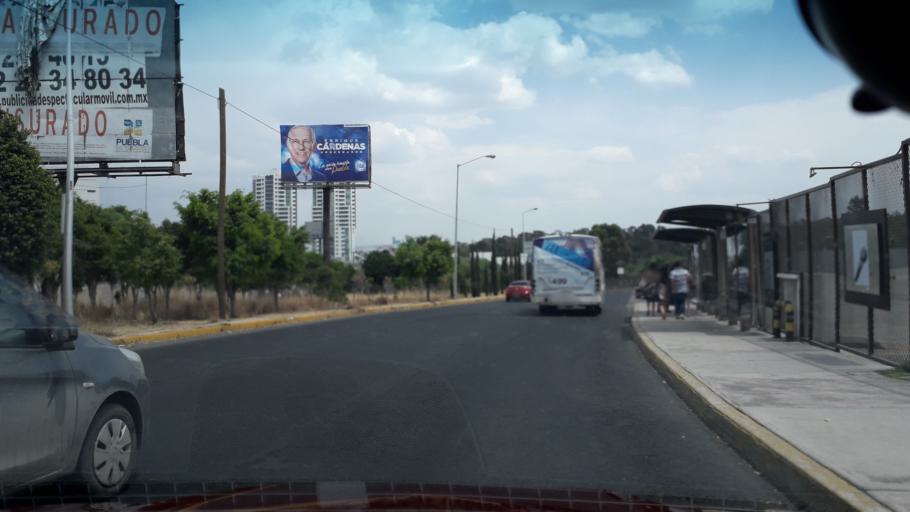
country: MX
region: Puebla
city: Puebla
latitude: 19.0210
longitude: -98.2390
